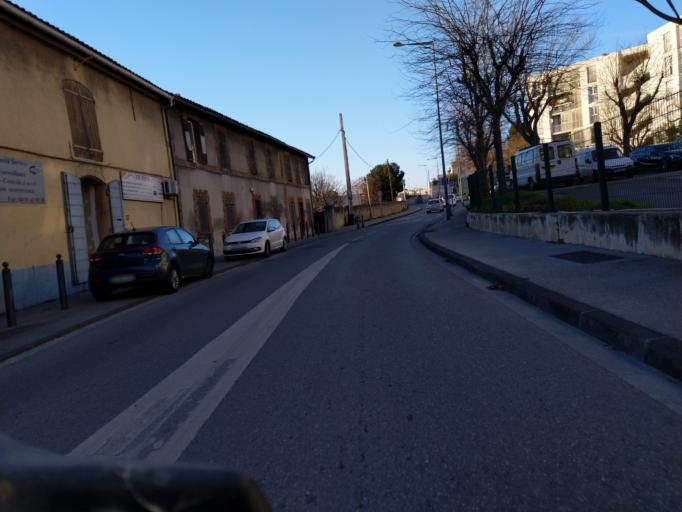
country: FR
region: Provence-Alpes-Cote d'Azur
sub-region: Departement des Bouches-du-Rhone
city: Marseille 12
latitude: 43.2912
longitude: 5.4262
